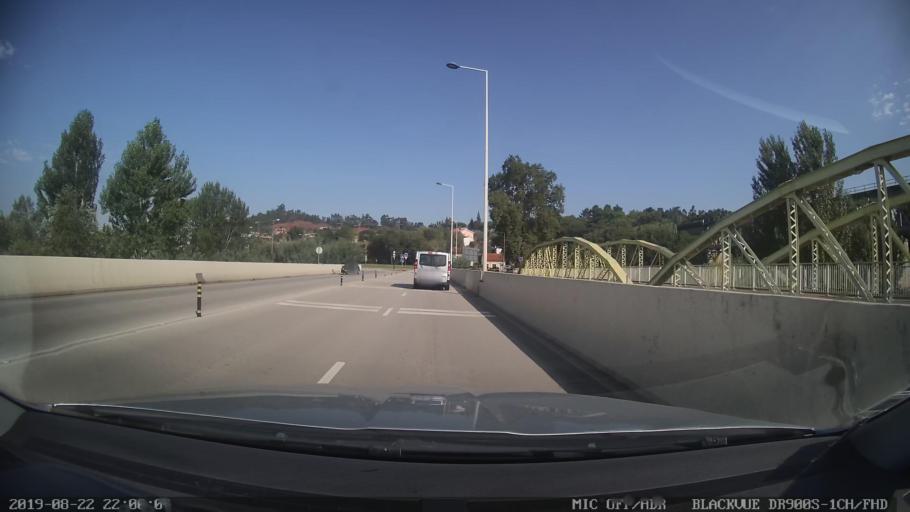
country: PT
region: Coimbra
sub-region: Coimbra
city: Coimbra
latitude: 40.1843
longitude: -8.3964
